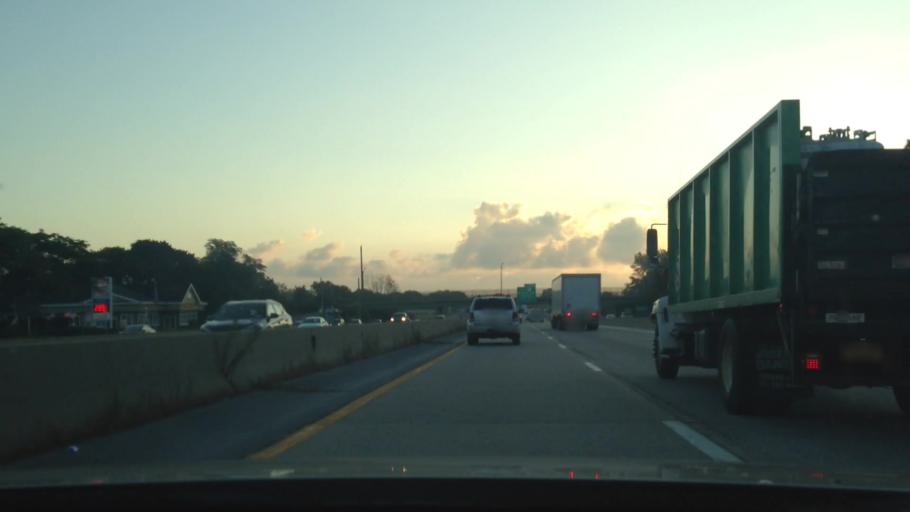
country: US
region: New York
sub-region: Suffolk County
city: North Great River
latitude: 40.7468
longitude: -73.1732
